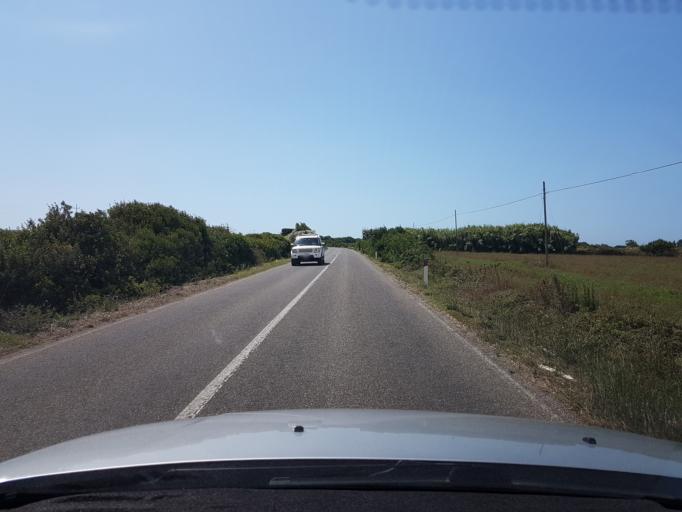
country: IT
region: Sardinia
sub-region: Provincia di Oristano
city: Riola Sardo
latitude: 40.0221
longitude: 8.4645
